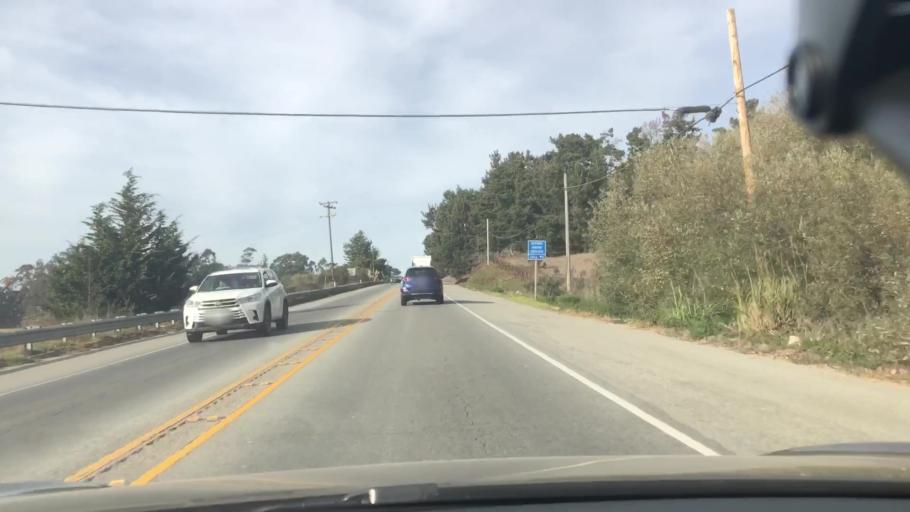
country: US
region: California
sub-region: Monterey County
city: Elkhorn
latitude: 36.8334
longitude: -121.7704
